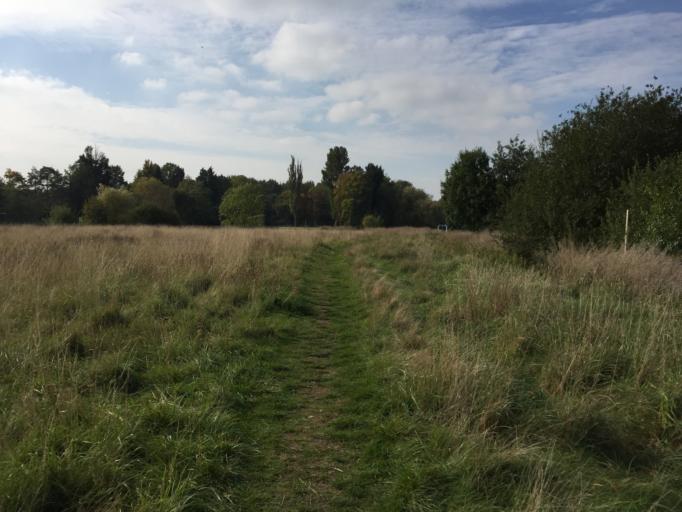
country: GB
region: England
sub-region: West Berkshire
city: Eton
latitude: 51.4887
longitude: -0.6260
